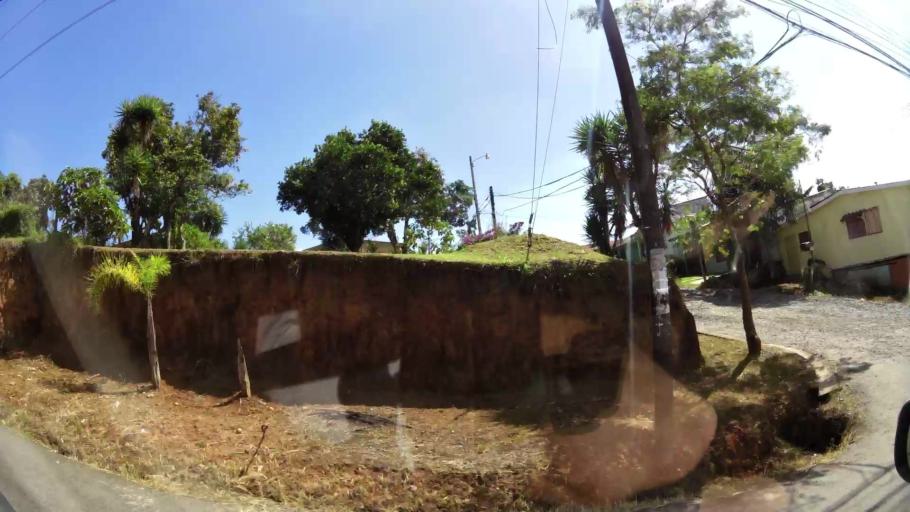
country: CR
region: San Jose
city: San Isidro
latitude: 9.3756
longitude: -83.6986
